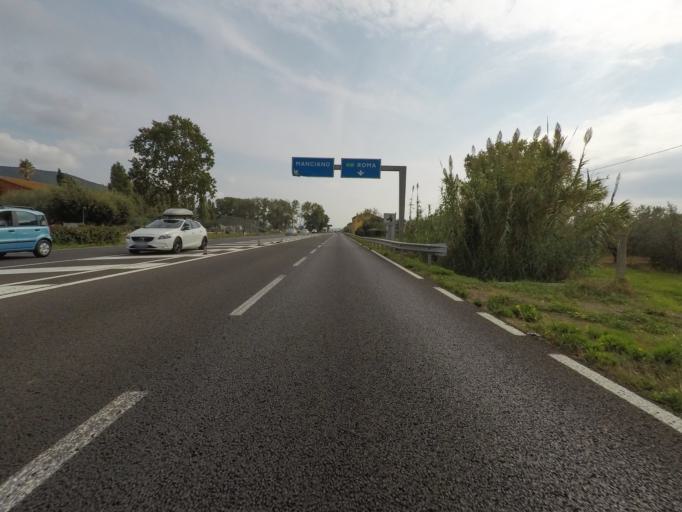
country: IT
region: Tuscany
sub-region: Provincia di Grosseto
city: Orbetello Scalo
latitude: 42.4729
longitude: 11.2347
